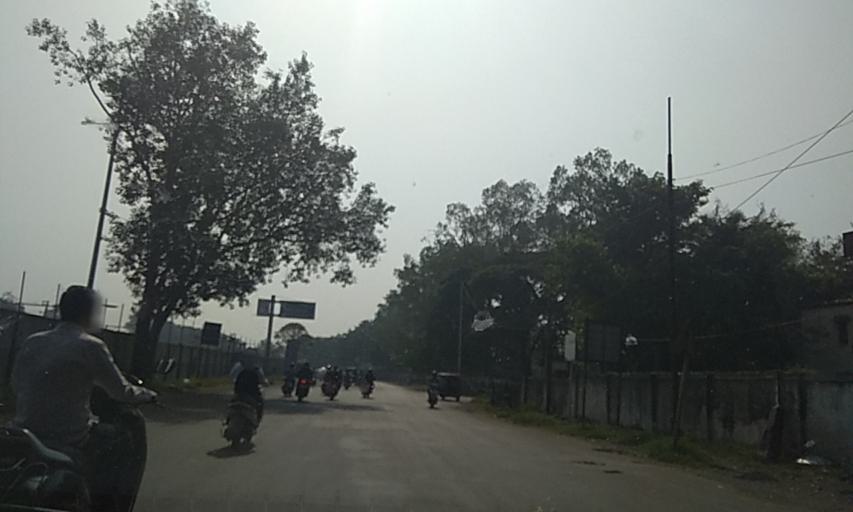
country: IN
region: Maharashtra
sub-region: Pune Division
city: Khadki
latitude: 18.5615
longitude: 73.8413
